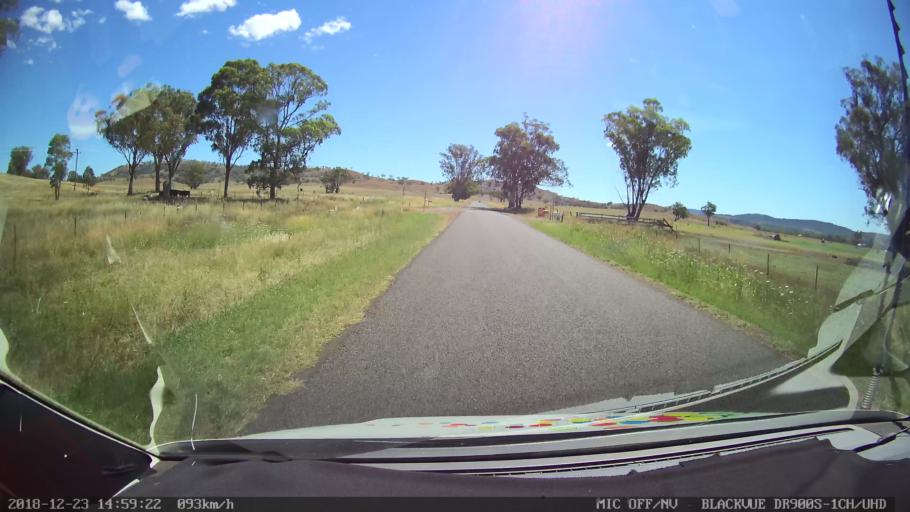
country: AU
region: New South Wales
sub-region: Tamworth Municipality
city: Manilla
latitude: -30.7234
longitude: 150.8015
